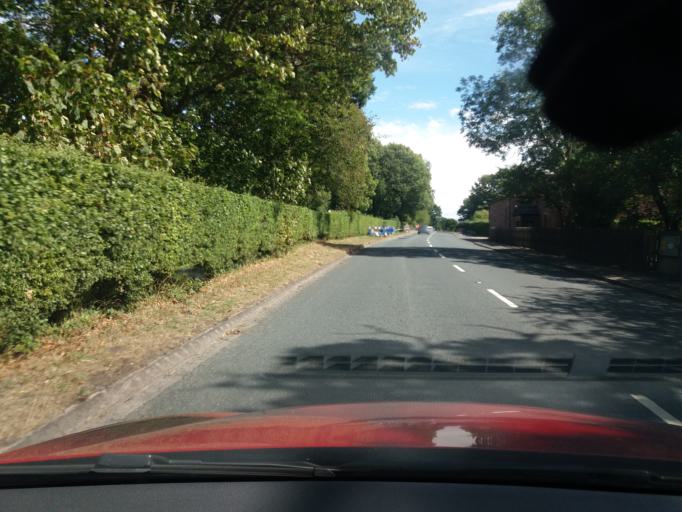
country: GB
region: England
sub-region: Lancashire
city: Euxton
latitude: 53.6591
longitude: -2.6934
